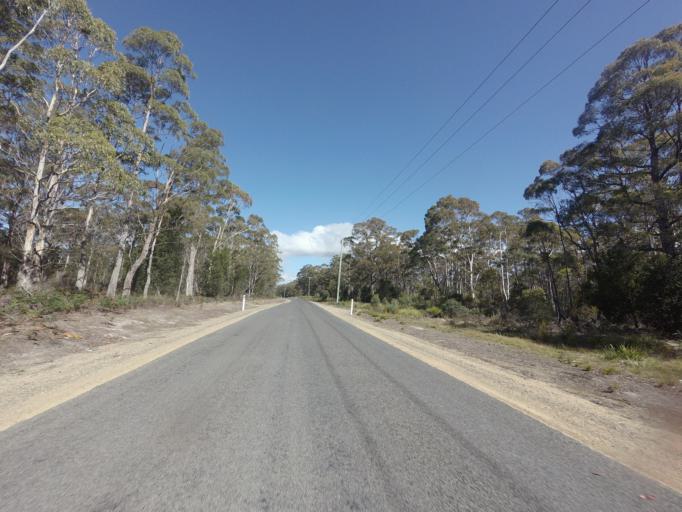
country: AU
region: Tasmania
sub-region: Break O'Day
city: St Helens
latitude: -41.6010
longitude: 148.2046
